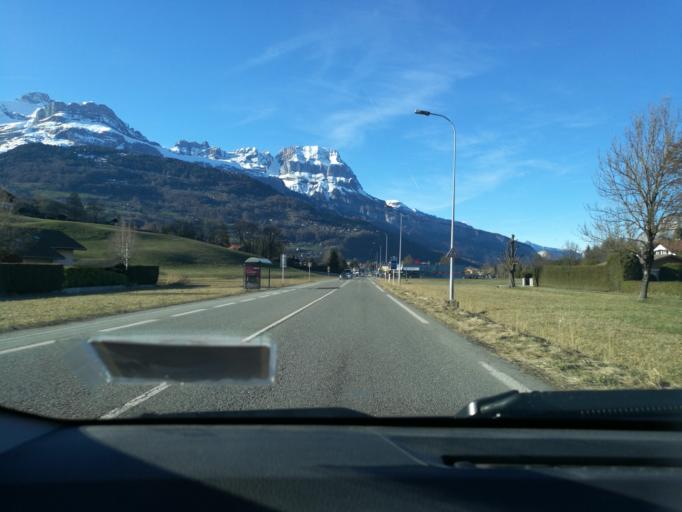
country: FR
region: Rhone-Alpes
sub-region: Departement de la Haute-Savoie
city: Domancy
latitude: 45.9236
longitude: 6.6426
